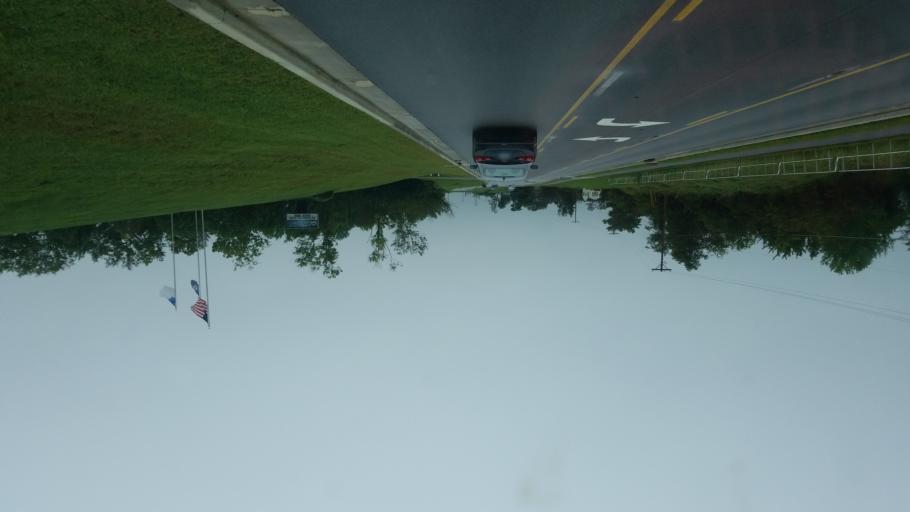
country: US
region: Ohio
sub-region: Brown County
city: Aberdeen
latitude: 38.6314
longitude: -83.7823
